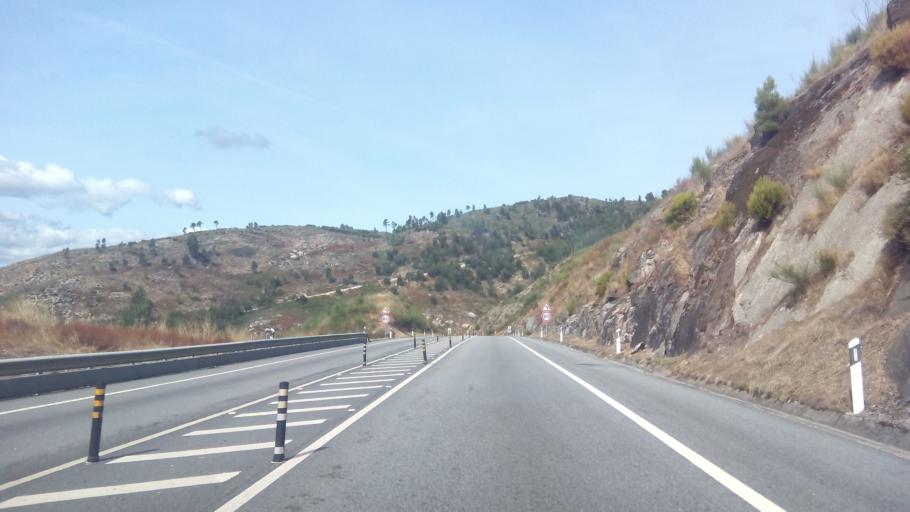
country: PT
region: Porto
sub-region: Amarante
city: Amarante
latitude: 41.2651
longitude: -7.9793
